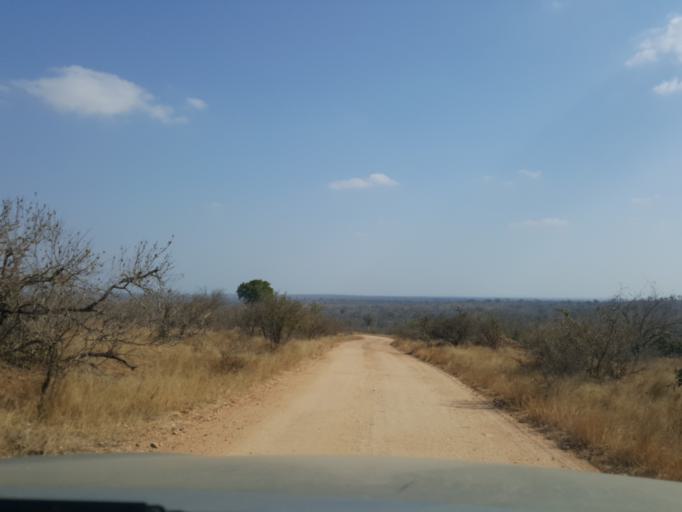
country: ZA
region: Mpumalanga
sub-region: Ehlanzeni District
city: Komatipoort
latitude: -25.3024
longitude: 31.7552
